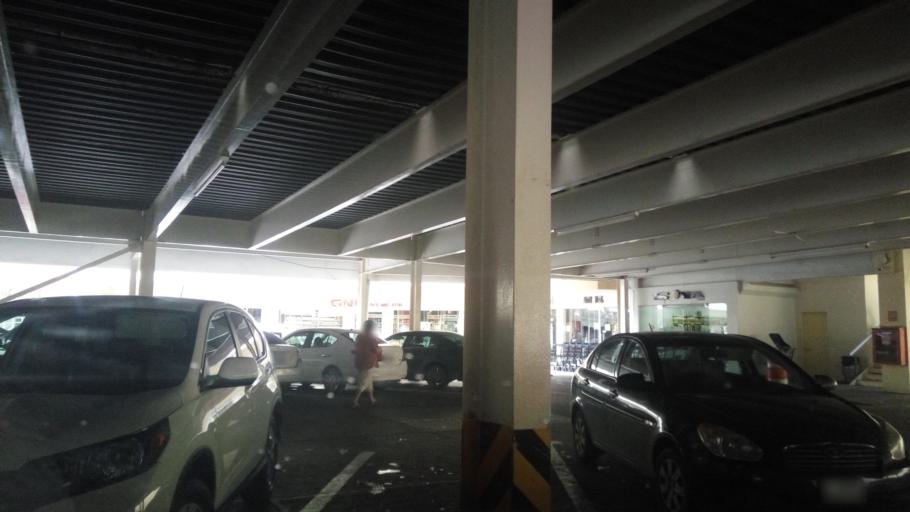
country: MX
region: Tabasco
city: Villahermosa
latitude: 17.9955
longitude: -92.9436
